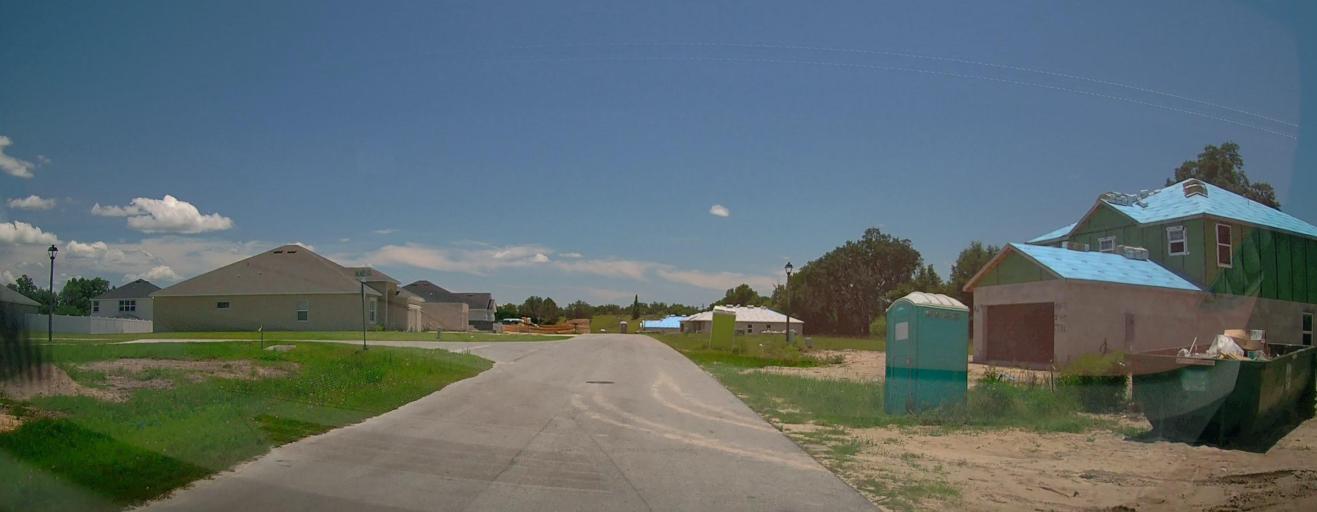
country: US
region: Florida
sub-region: Marion County
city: Belleview
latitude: 29.0905
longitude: -82.0780
